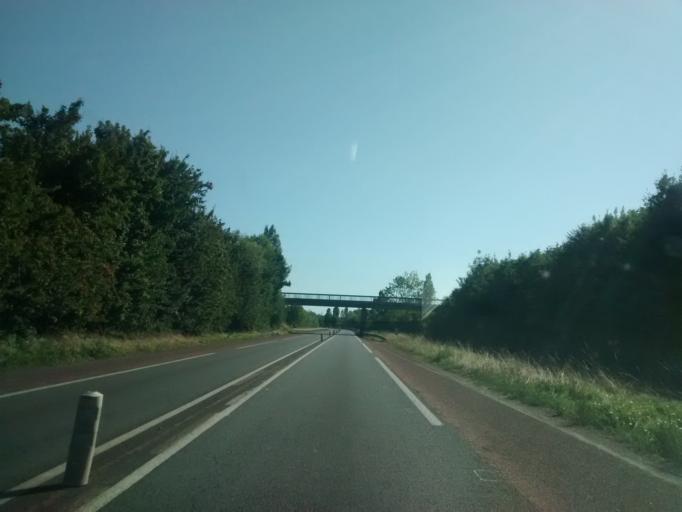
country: FR
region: Aquitaine
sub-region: Departement de la Gironde
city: Genissac
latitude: 44.8698
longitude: -0.2384
